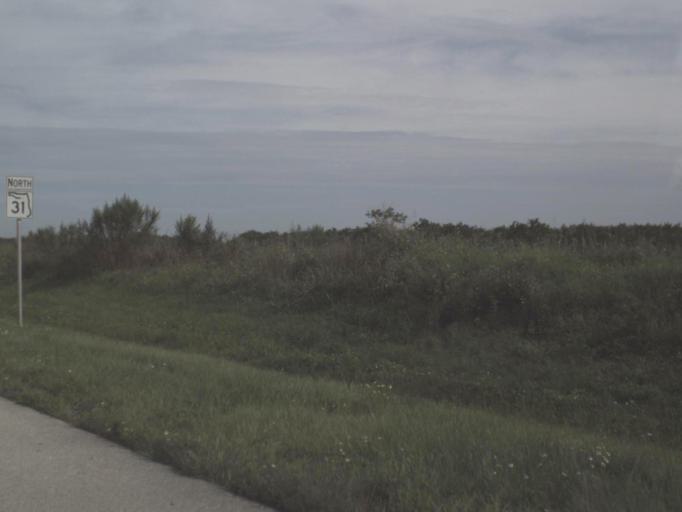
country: US
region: Florida
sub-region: DeSoto County
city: Nocatee
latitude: 27.0636
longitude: -81.7913
